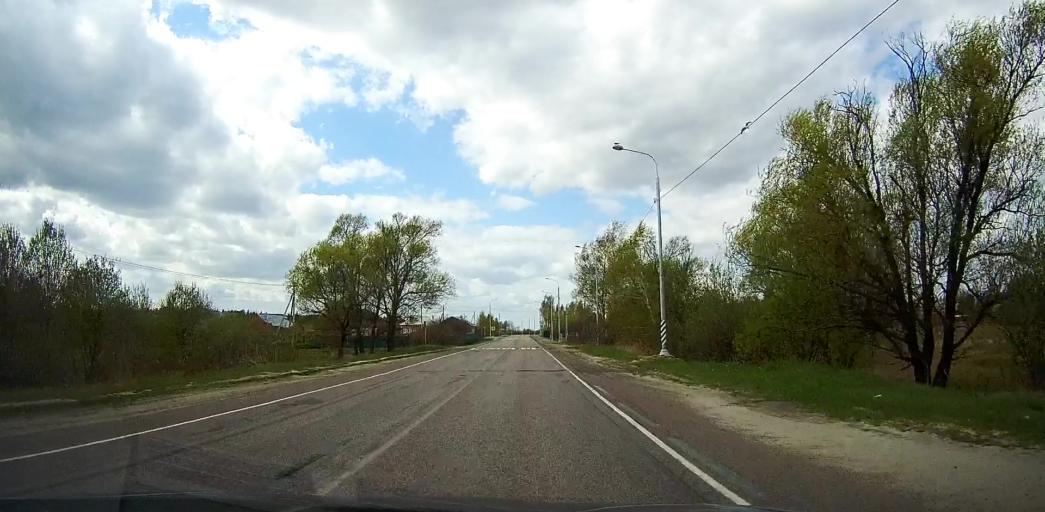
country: RU
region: Moskovskaya
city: Davydovo
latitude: 55.6643
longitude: 38.8023
